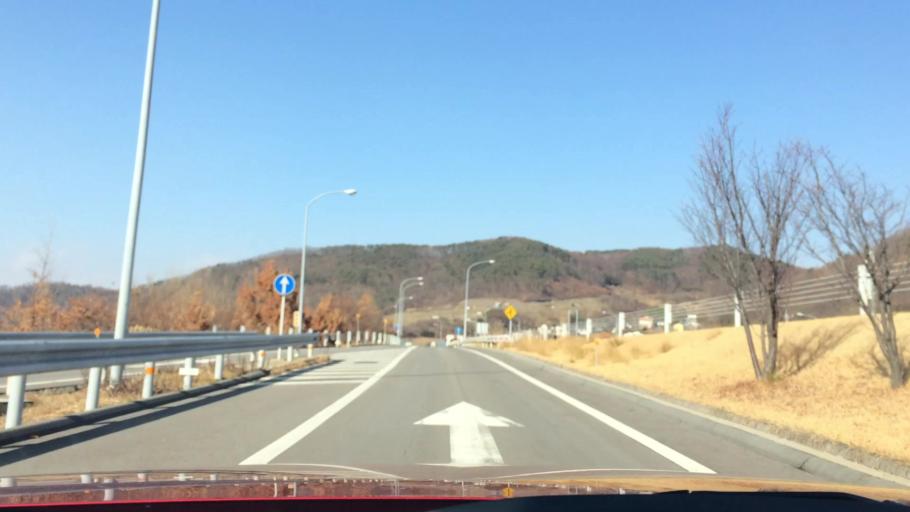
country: JP
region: Nagano
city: Ueda
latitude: 36.3735
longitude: 138.3464
